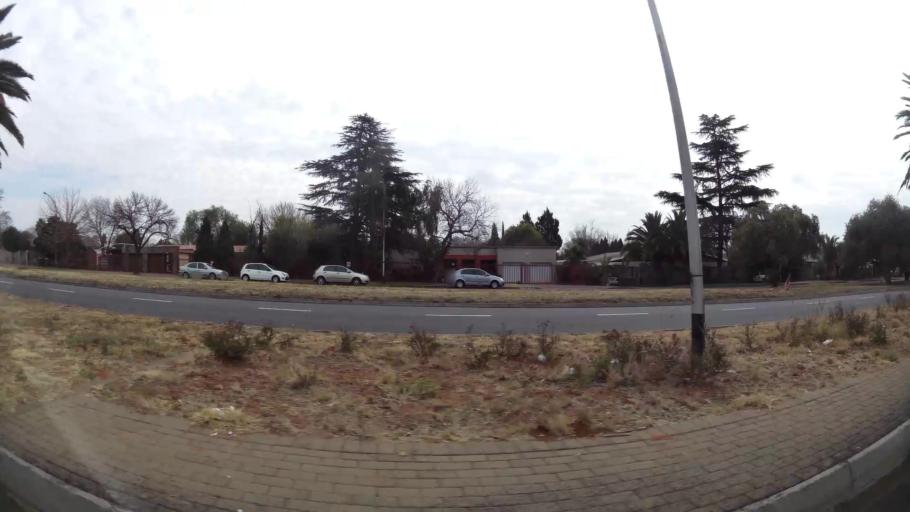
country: ZA
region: Orange Free State
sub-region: Mangaung Metropolitan Municipality
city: Bloemfontein
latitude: -29.1265
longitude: 26.1756
